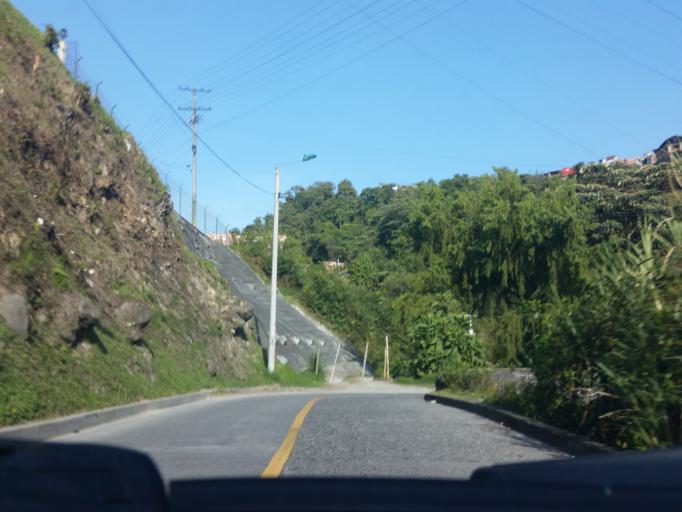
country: CO
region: Caldas
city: Manizales
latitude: 5.0702
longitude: -75.4957
